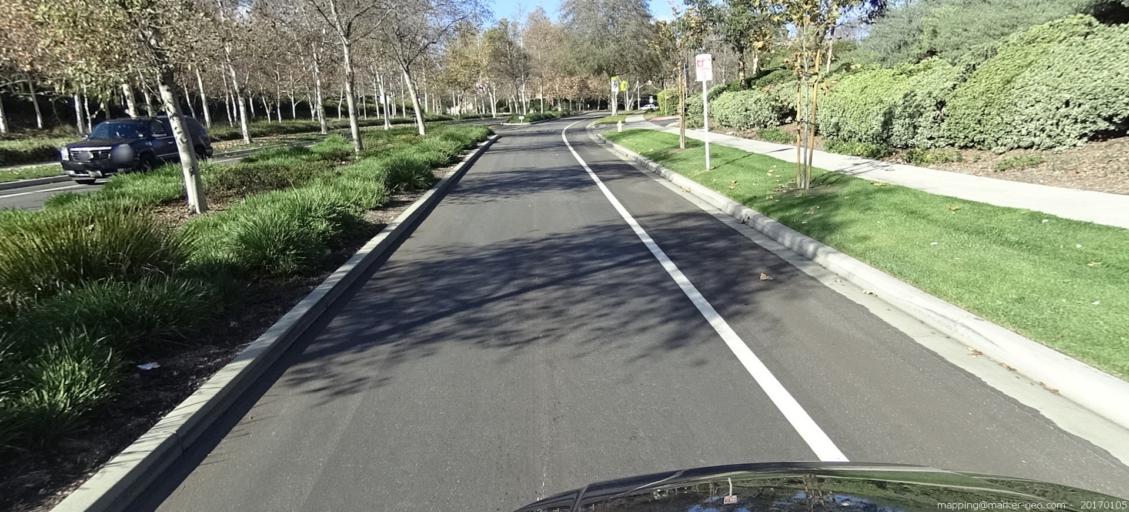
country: US
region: California
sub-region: Orange County
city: Ladera Ranch
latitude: 33.5594
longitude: -117.6361
